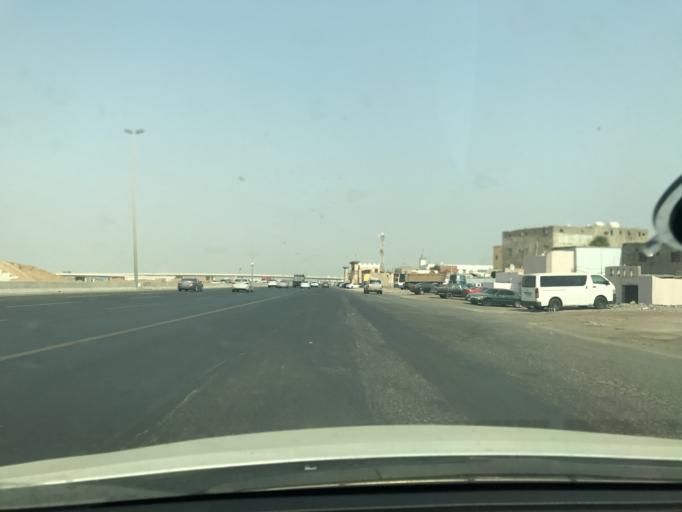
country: SA
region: Makkah
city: Jeddah
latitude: 21.6332
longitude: 39.1664
